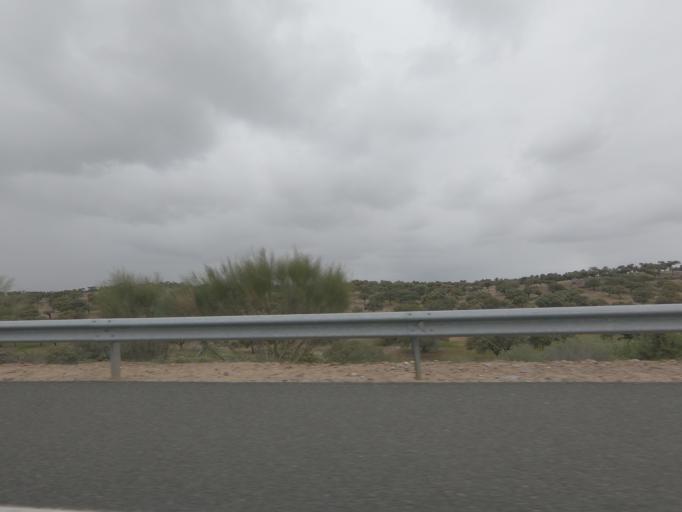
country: ES
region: Extremadura
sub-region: Provincia de Caceres
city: Plasencia
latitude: 40.0659
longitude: -6.1140
